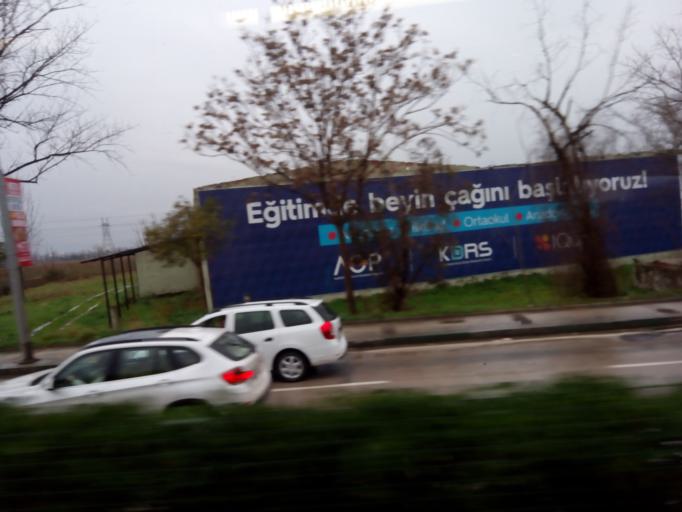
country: TR
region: Bursa
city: Yildirim
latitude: 40.2114
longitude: 29.0226
